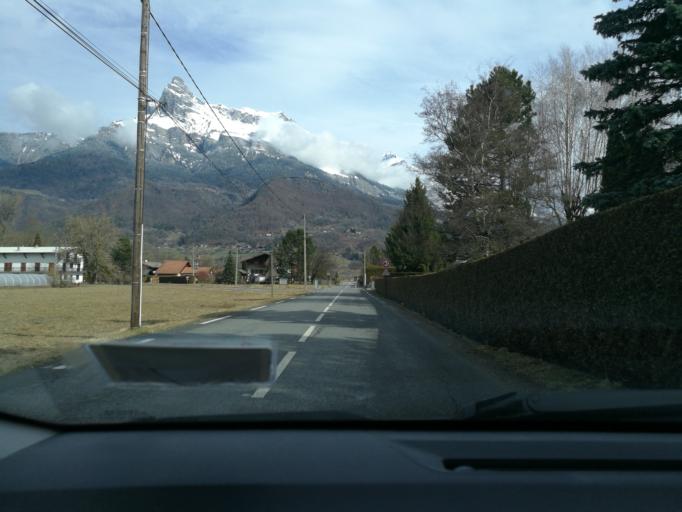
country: FR
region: Rhone-Alpes
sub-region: Departement de la Haute-Savoie
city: Domancy
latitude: 45.9127
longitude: 6.6576
